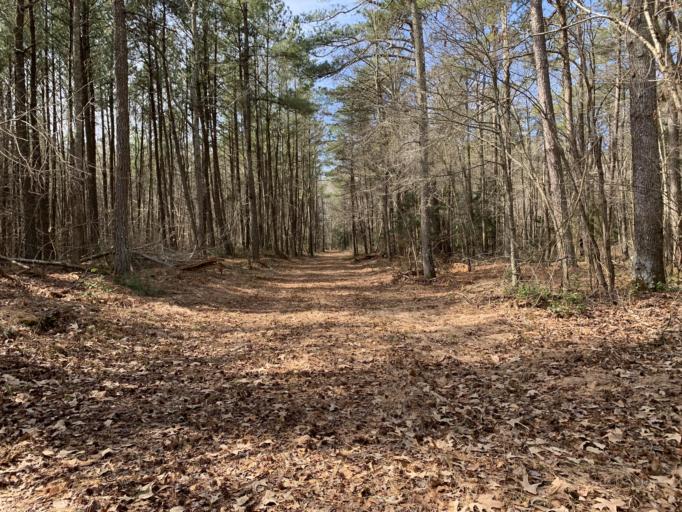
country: US
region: Delaware
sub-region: Sussex County
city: Georgetown
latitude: 38.7403
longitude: -75.3783
